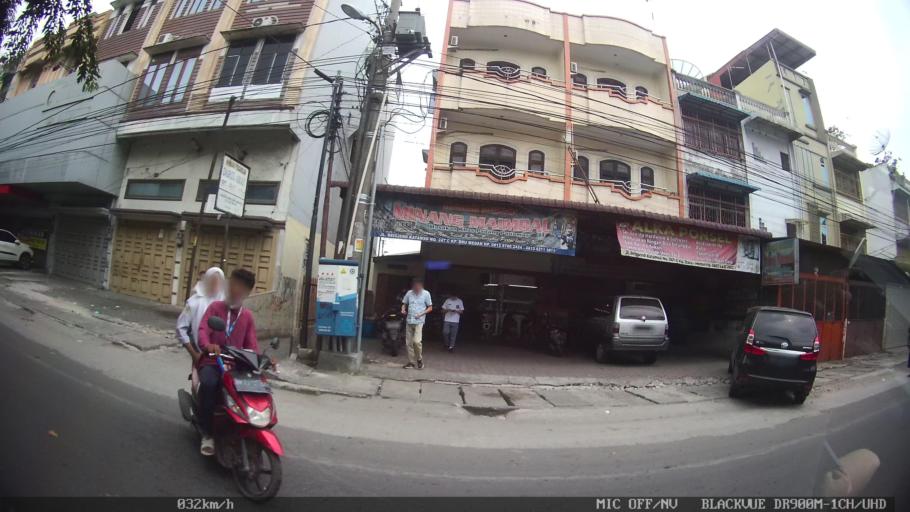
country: ID
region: North Sumatra
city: Medan
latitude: 3.5588
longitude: 98.6889
